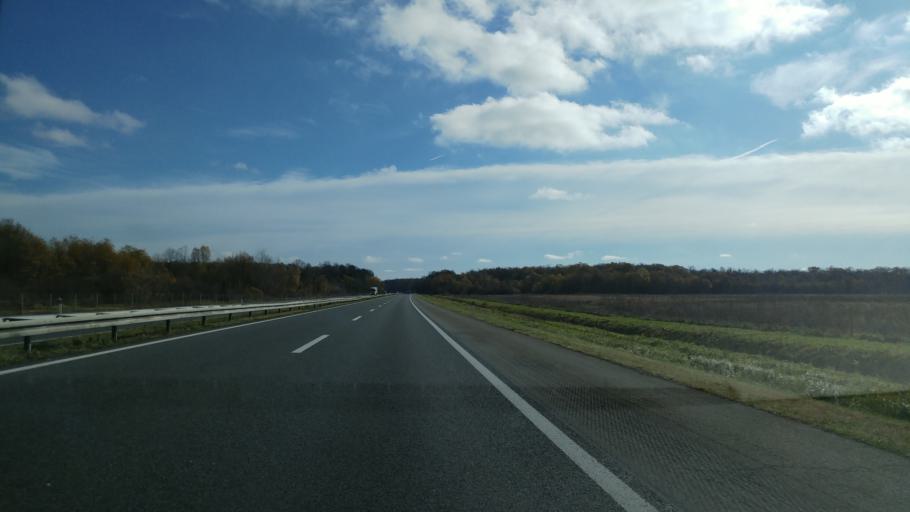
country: HR
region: Sisacko-Moslavacka
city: Lipovljani
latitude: 45.3501
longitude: 16.9130
